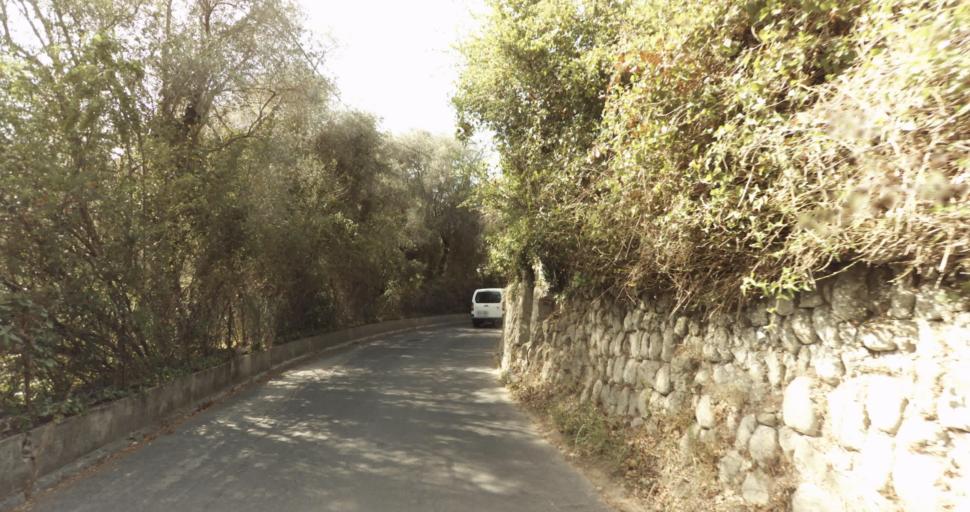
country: FR
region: Provence-Alpes-Cote d'Azur
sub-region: Departement des Alpes-Maritimes
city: Sainte-Agnes
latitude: 43.7903
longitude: 7.4815
